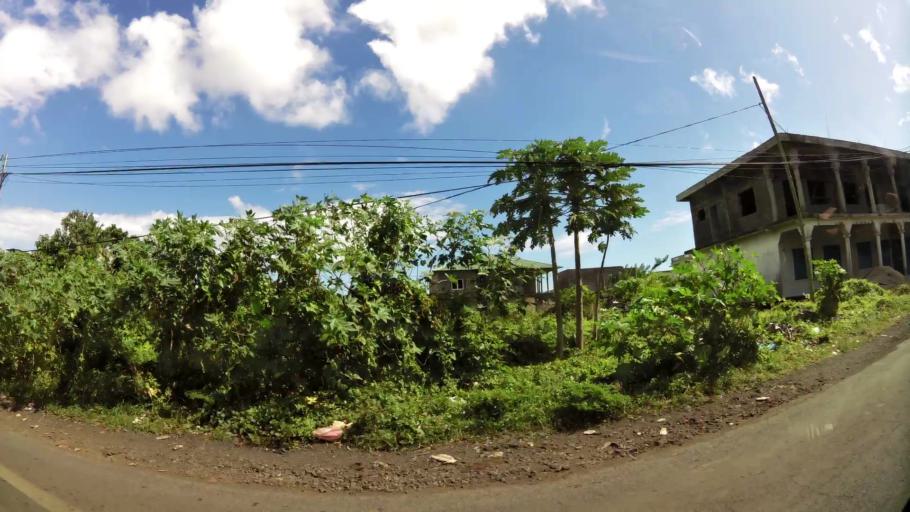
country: KM
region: Grande Comore
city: Mavingouni
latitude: -11.7257
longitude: 43.2493
